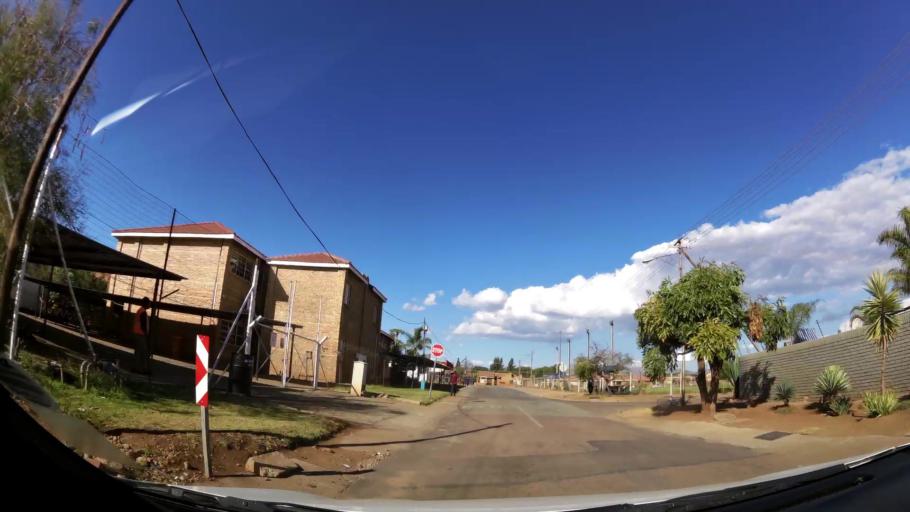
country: ZA
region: Limpopo
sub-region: Waterberg District Municipality
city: Mokopane
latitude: -24.1772
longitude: 28.9982
